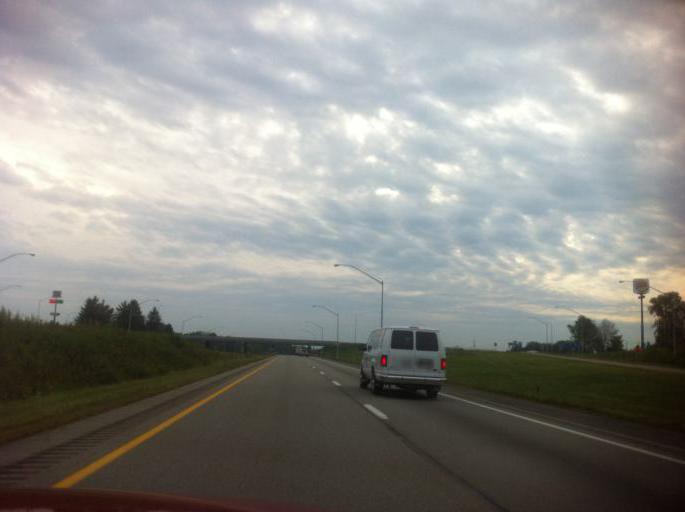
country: US
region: Pennsylvania
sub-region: Mercer County
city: Grove City
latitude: 41.2018
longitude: -79.9707
